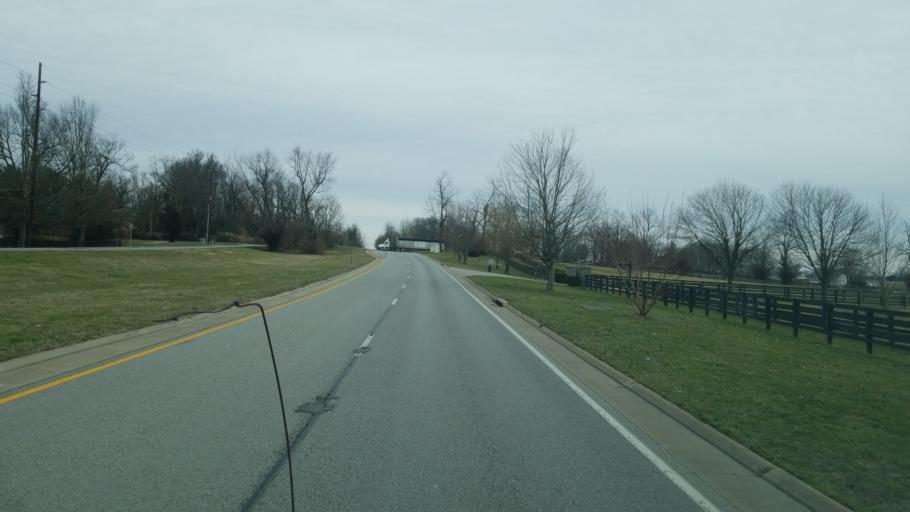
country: US
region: Kentucky
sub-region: Fayette County
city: Lexington-Fayette
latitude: 38.0933
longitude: -84.4281
